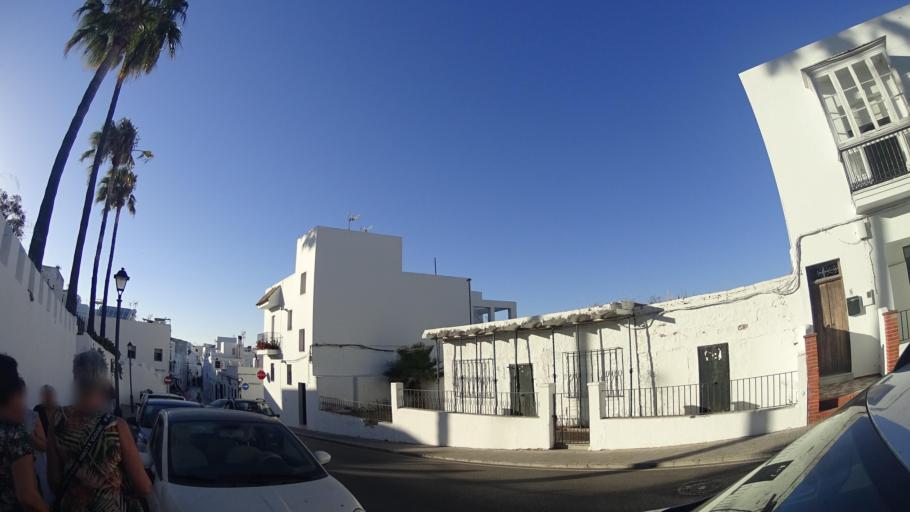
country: ES
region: Andalusia
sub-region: Provincia de Cadiz
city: Vejer de la Frontera
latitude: 36.2515
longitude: -5.9660
